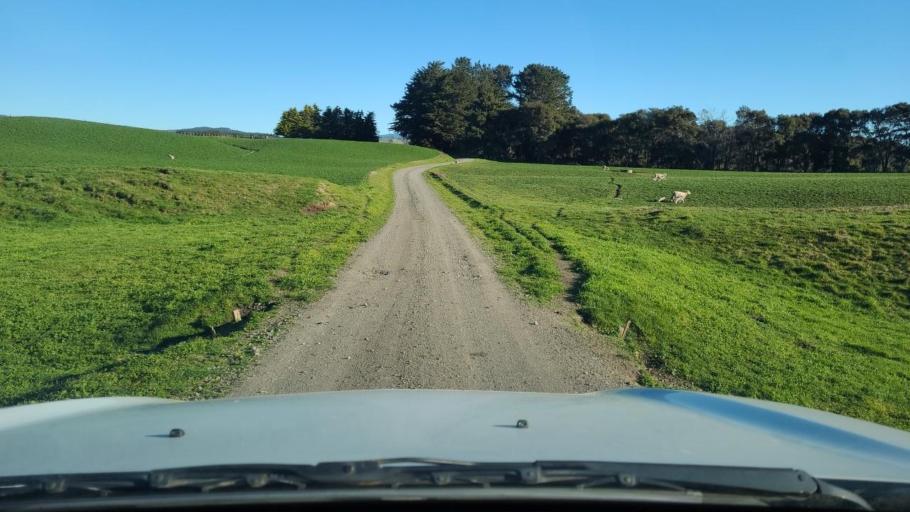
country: NZ
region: Hawke's Bay
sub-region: Napier City
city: Taradale
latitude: -39.4188
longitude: 176.5424
